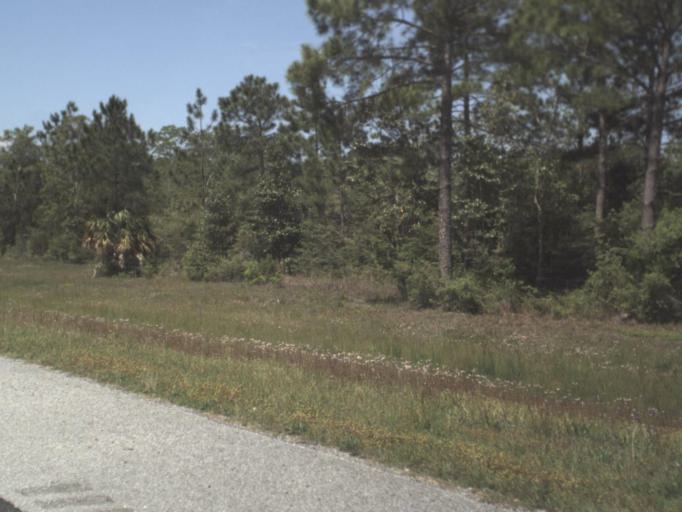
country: US
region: Florida
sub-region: Santa Rosa County
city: Bagdad
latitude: 30.5372
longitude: -87.0742
